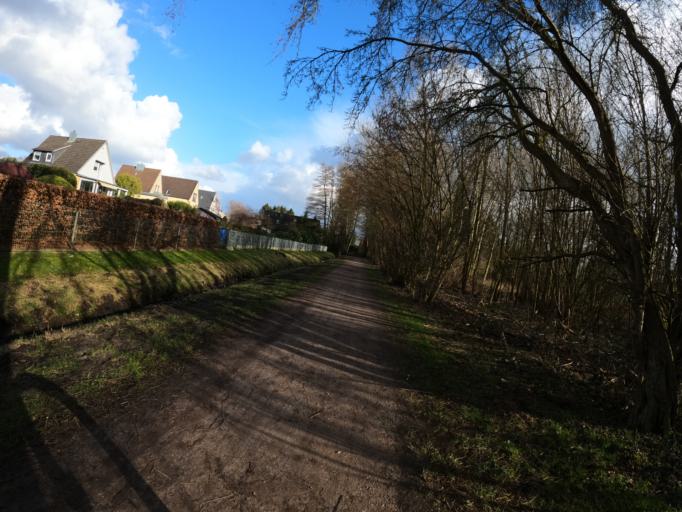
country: DE
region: Schleswig-Holstein
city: Bonningstedt
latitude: 53.6382
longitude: 9.9361
